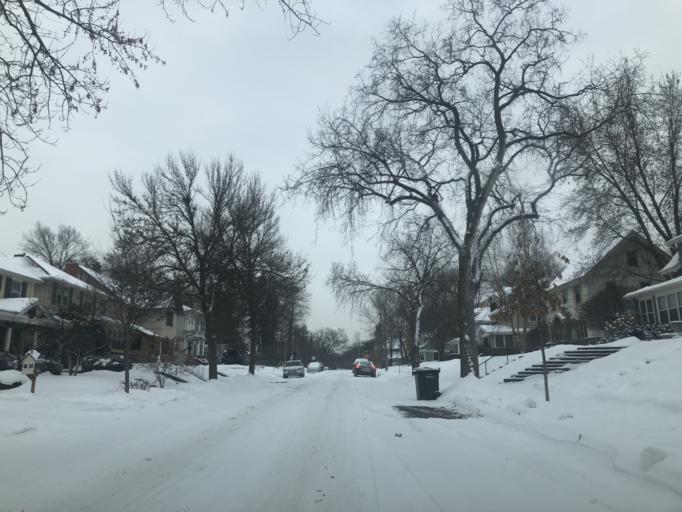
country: US
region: Minnesota
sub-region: Hennepin County
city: Richfield
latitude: 44.9224
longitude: -93.2922
